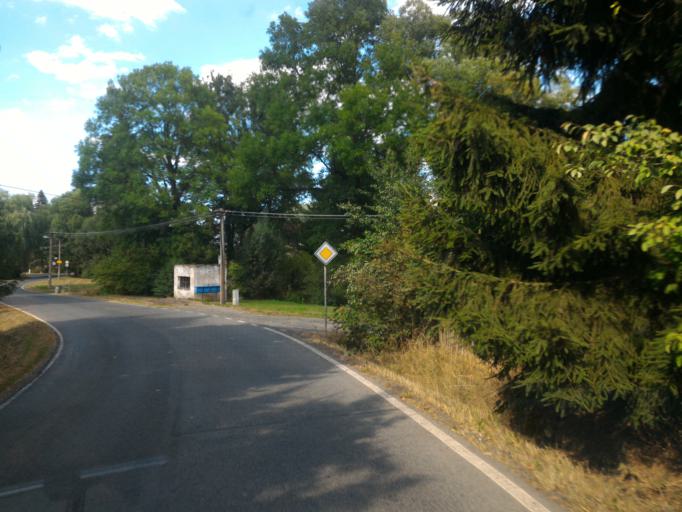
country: CZ
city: Jablonne v Podjestedi
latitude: 50.7895
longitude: 14.7348
